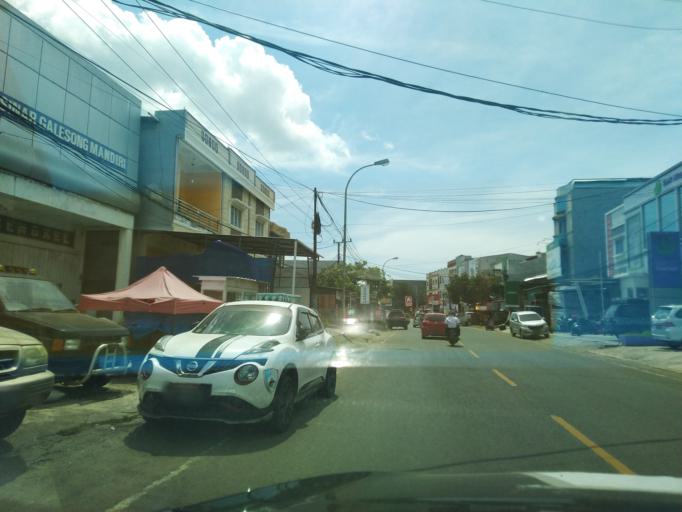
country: ID
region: Sulawesi Barat
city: Mamuju
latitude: -2.6794
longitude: 118.8787
